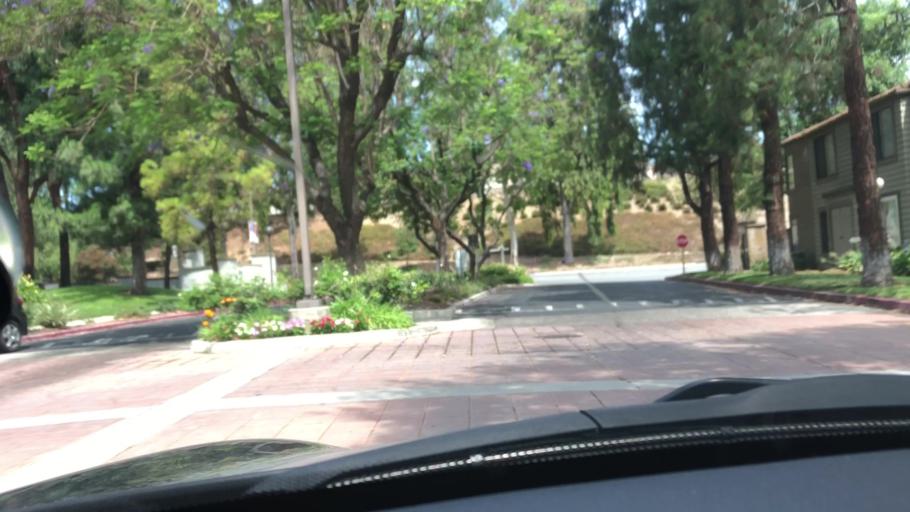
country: US
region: California
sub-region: Los Angeles County
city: Pomona
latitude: 34.0259
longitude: -117.7654
